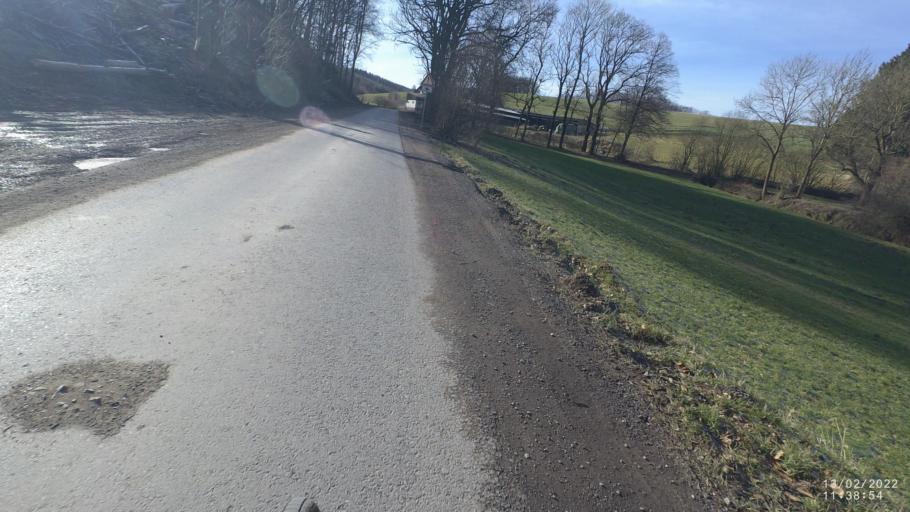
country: DE
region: North Rhine-Westphalia
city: Neuenrade
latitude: 51.3172
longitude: 7.7713
